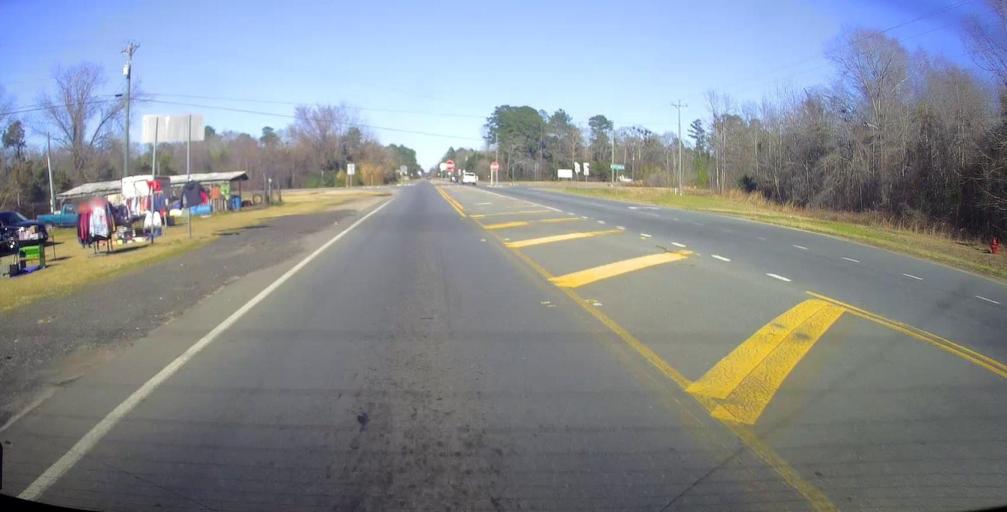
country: US
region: Georgia
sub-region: Macon County
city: Oglethorpe
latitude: 32.2688
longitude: -84.0824
